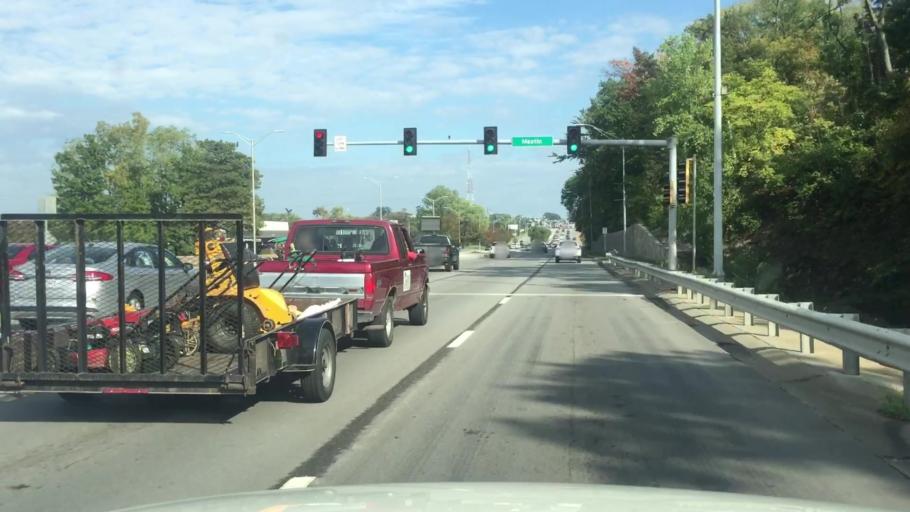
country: US
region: Kansas
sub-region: Johnson County
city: Merriam
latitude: 39.0147
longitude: -94.7043
